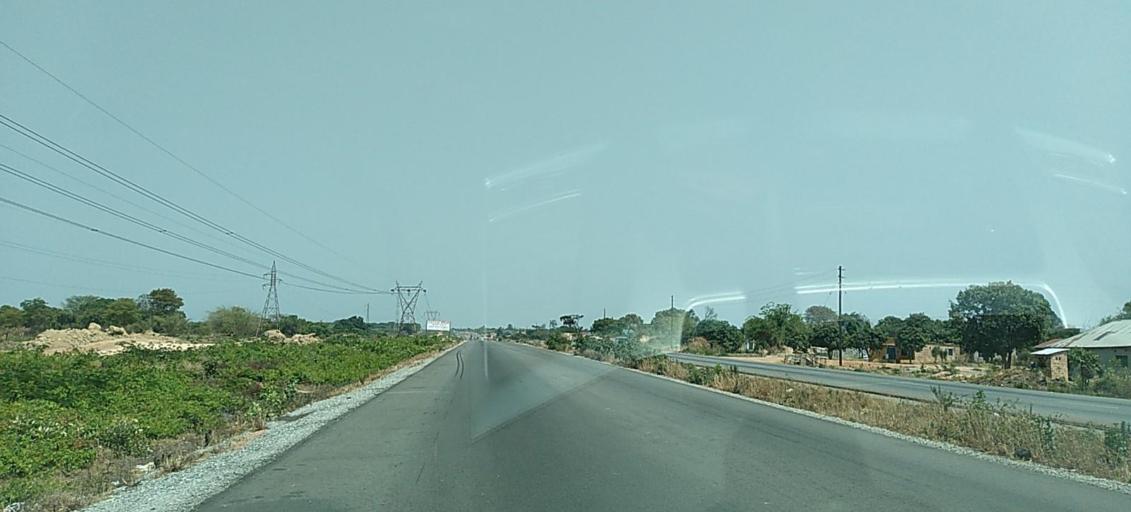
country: ZM
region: Copperbelt
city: Chambishi
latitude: -12.6020
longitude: 27.9668
